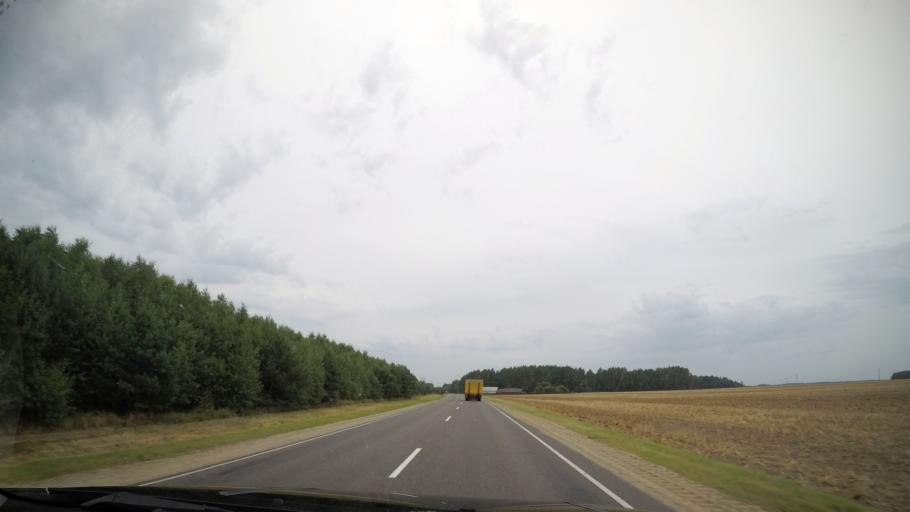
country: BY
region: Grodnenskaya
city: Iwye
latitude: 53.8993
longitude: 25.7513
